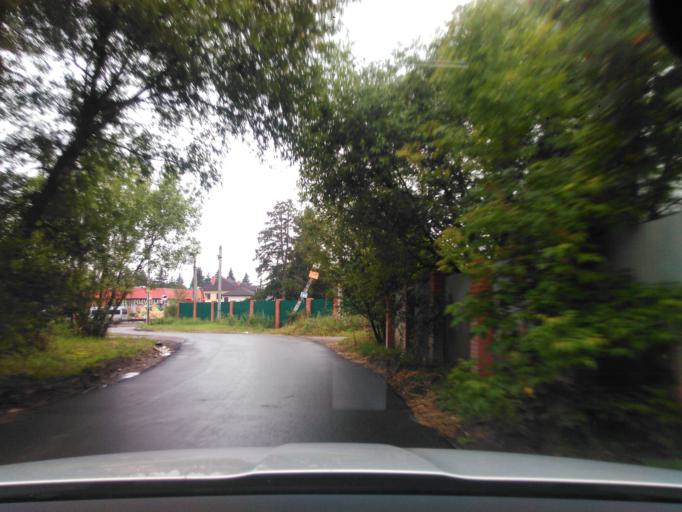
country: RU
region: Moskovskaya
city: Firsanovka
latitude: 55.9506
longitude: 37.2381
